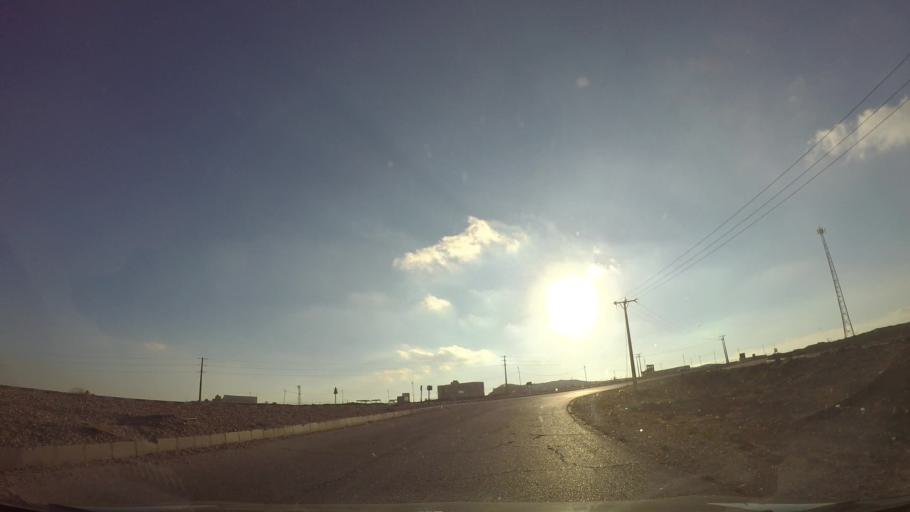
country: JO
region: Tafielah
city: Busayra
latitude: 30.4987
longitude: 35.7982
